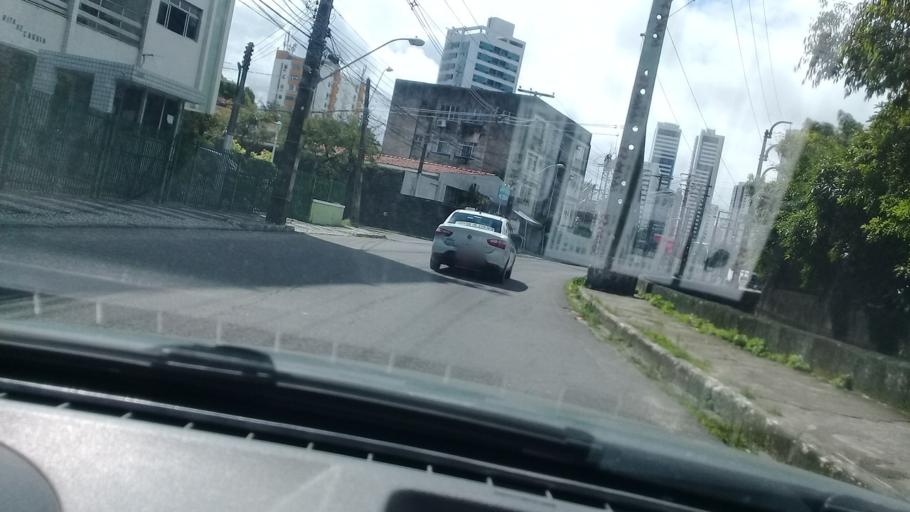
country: BR
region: Pernambuco
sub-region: Recife
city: Recife
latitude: -8.0627
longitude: -34.9050
